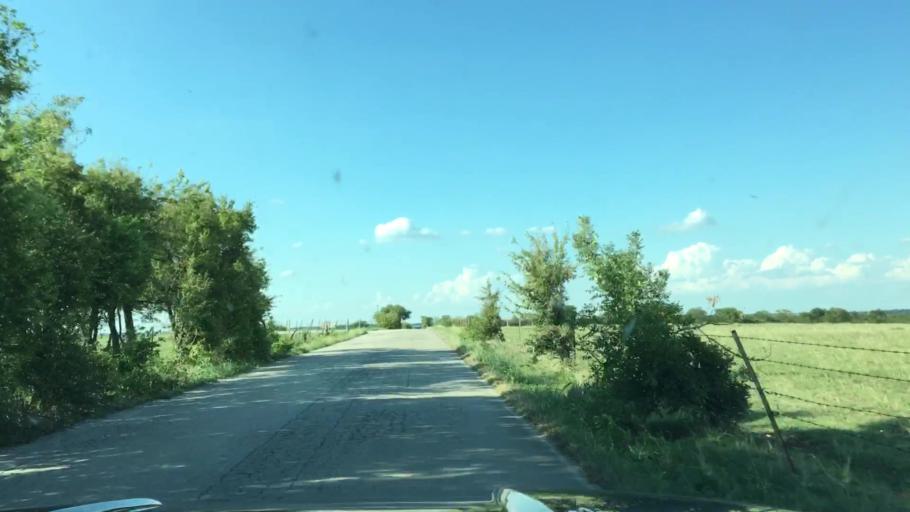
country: US
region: Texas
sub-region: Tarrant County
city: Haslet
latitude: 33.0198
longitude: -97.3767
